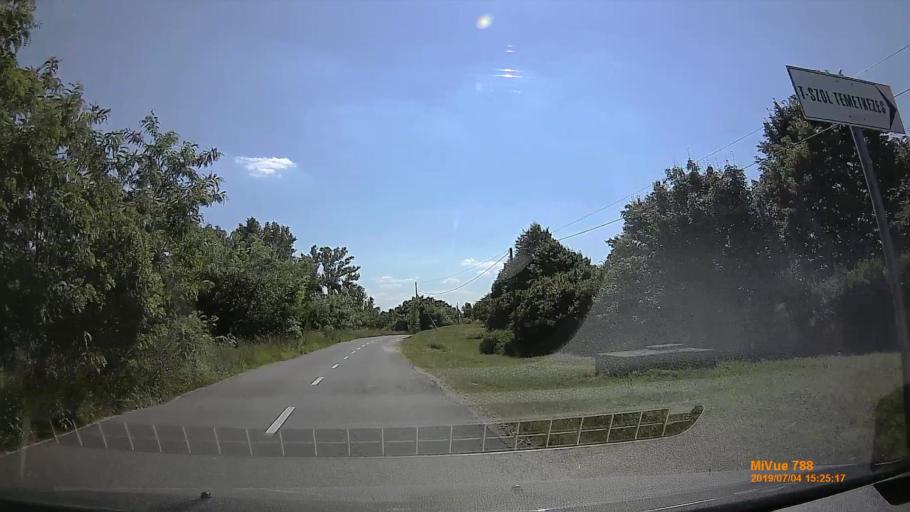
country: HU
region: Komarom-Esztergom
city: Tatabanya
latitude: 47.5566
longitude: 18.3830
